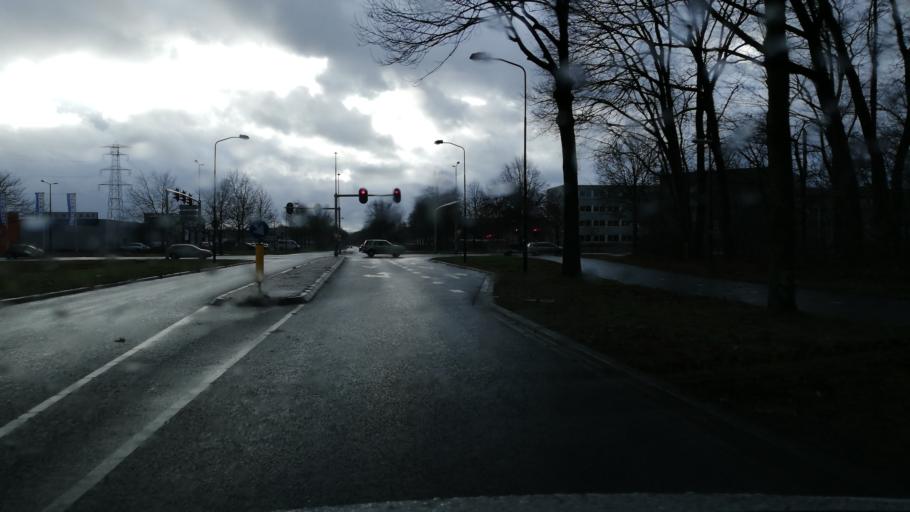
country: NL
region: Gelderland
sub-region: Gemeente Apeldoorn
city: Beekbergen
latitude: 52.1797
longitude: 5.9699
